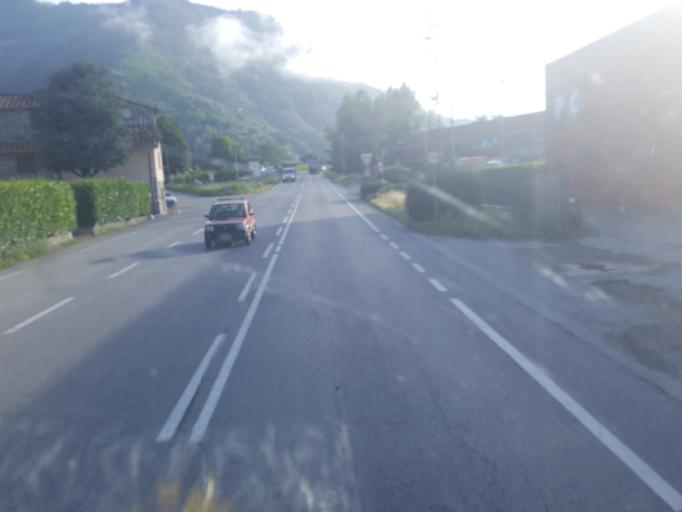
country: IT
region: Tuscany
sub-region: Provincia di Lucca
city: Valdottavo
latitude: 43.9564
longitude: 10.5033
